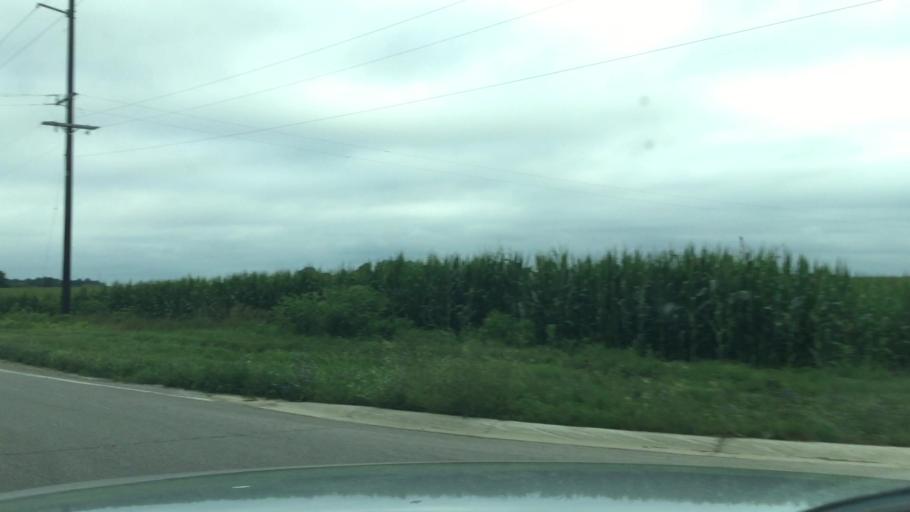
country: US
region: Michigan
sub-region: Montcalm County
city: Greenville
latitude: 43.1924
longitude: -85.2232
